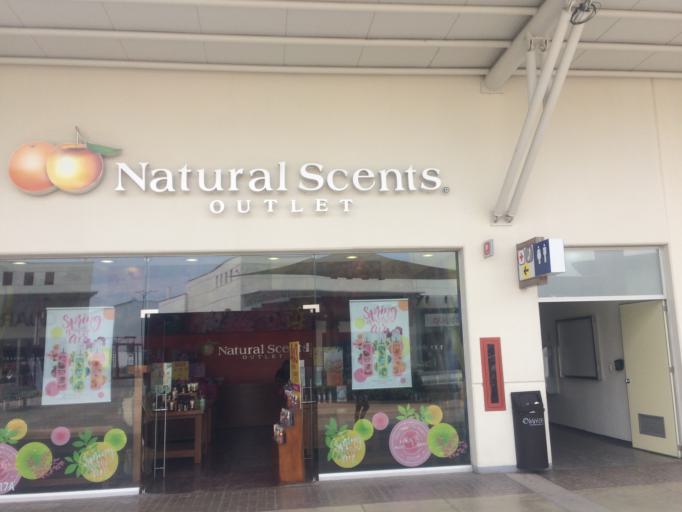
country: MX
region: Guanajuato
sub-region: Leon
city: Fraccionamiento Paraiso Real
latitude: 21.0881
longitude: -101.6154
